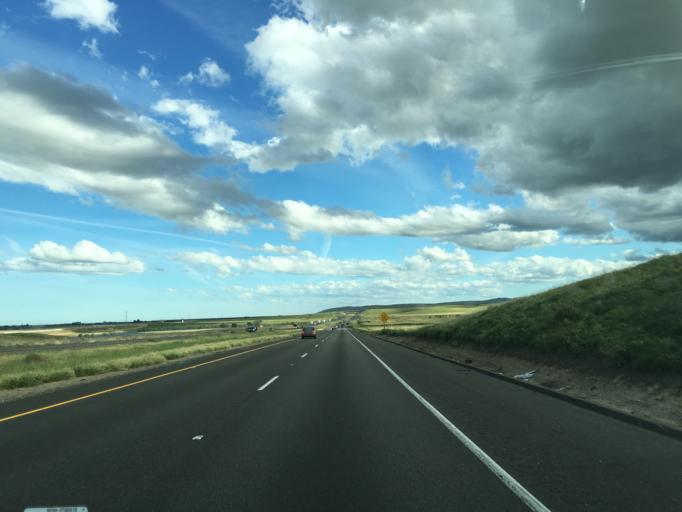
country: US
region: California
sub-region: Merced County
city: Los Banos
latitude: 37.0079
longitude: -120.9229
